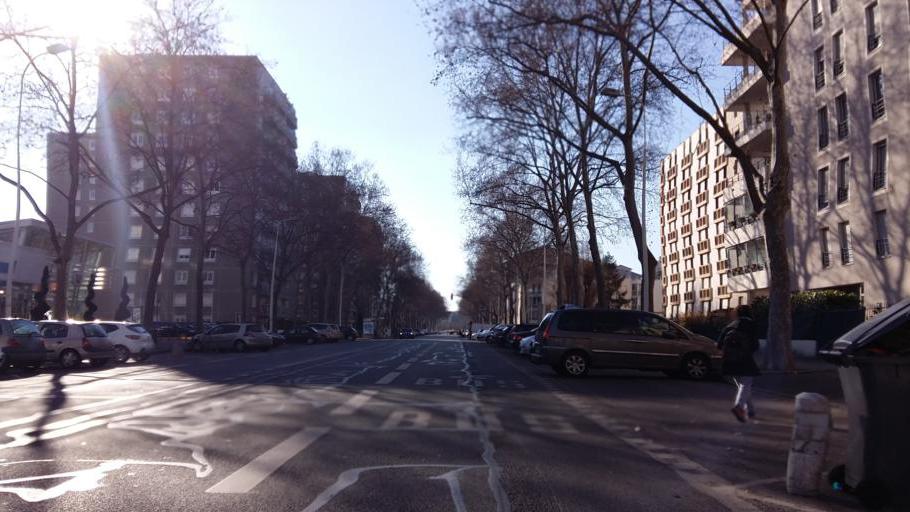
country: FR
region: Rhone-Alpes
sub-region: Departement du Rhone
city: Lyon
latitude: 45.7368
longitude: 4.8285
